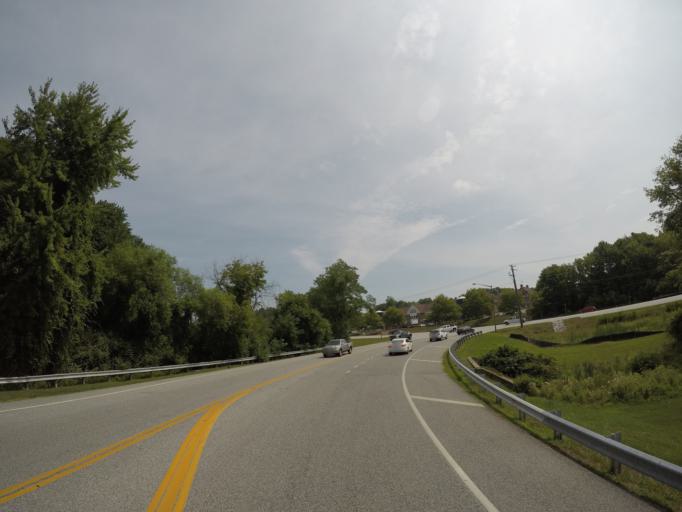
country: US
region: Maryland
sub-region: Howard County
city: Columbia
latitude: 39.3081
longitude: -76.8996
